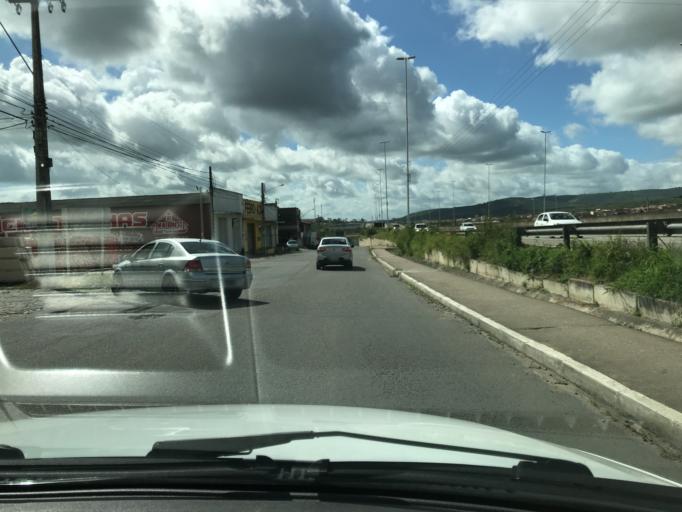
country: BR
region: Pernambuco
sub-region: Bezerros
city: Bezerros
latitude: -8.2380
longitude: -35.7440
